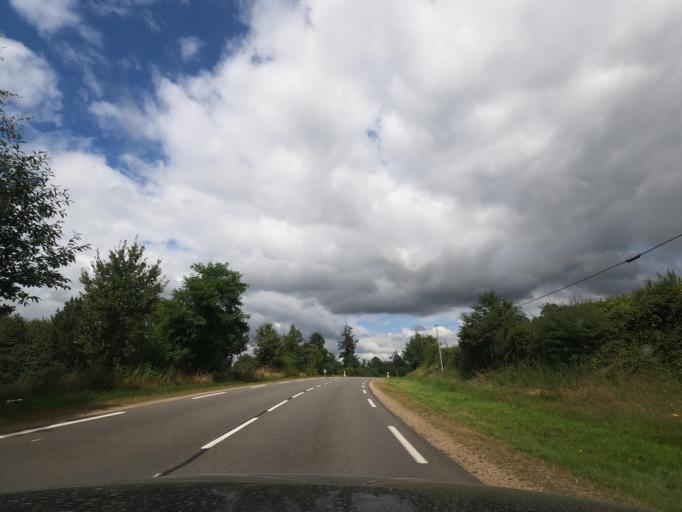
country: FR
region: Lower Normandy
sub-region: Departement de l'Orne
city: Champsecret
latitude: 48.6406
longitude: -0.5493
